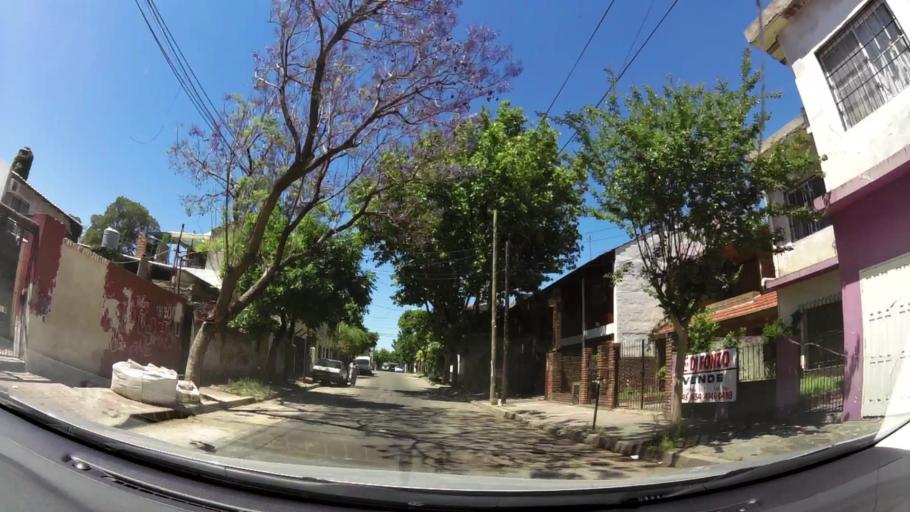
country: AR
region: Buenos Aires
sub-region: Partido de Tigre
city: Tigre
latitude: -34.4523
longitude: -58.5494
